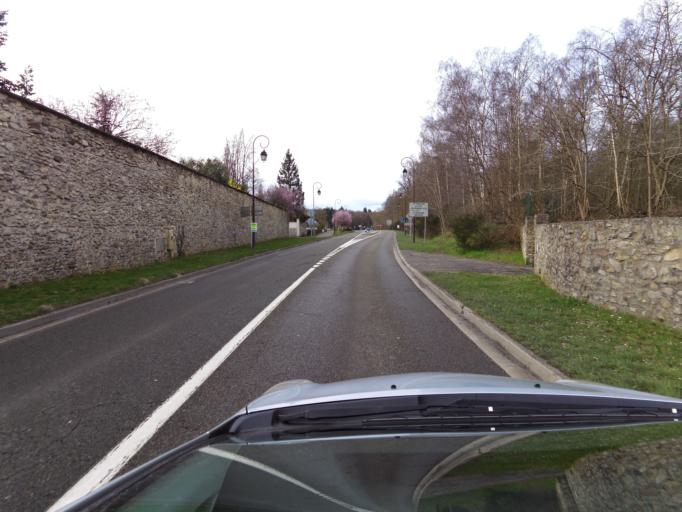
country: FR
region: Picardie
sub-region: Departement de l'Oise
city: Ver-sur-Launette
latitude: 49.1302
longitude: 2.6909
